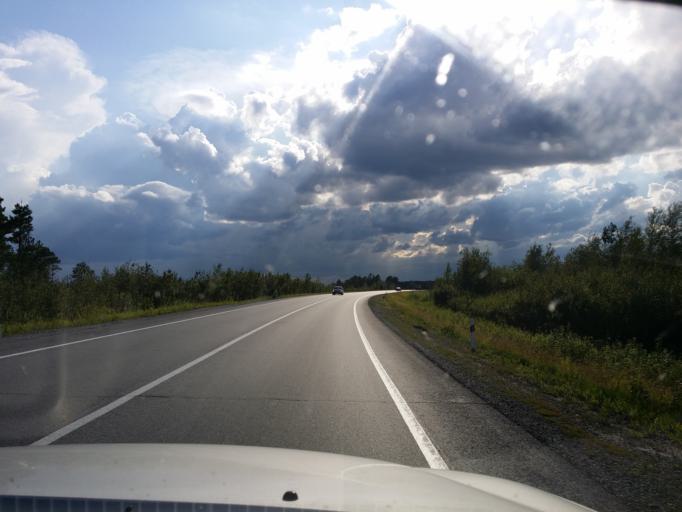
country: RU
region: Khanty-Mansiyskiy Avtonomnyy Okrug
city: Surgut
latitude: 61.4518
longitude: 74.0466
